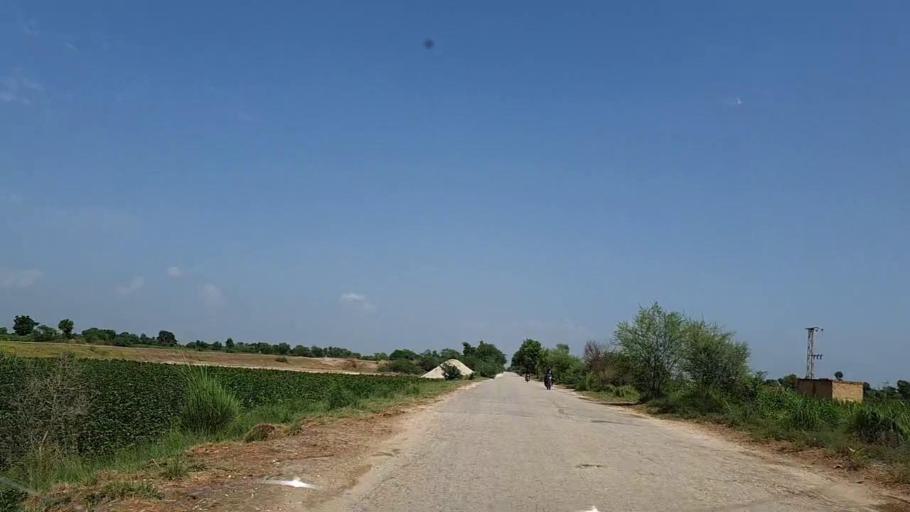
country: PK
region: Sindh
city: Naushahro Firoz
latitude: 26.8074
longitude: 68.2063
